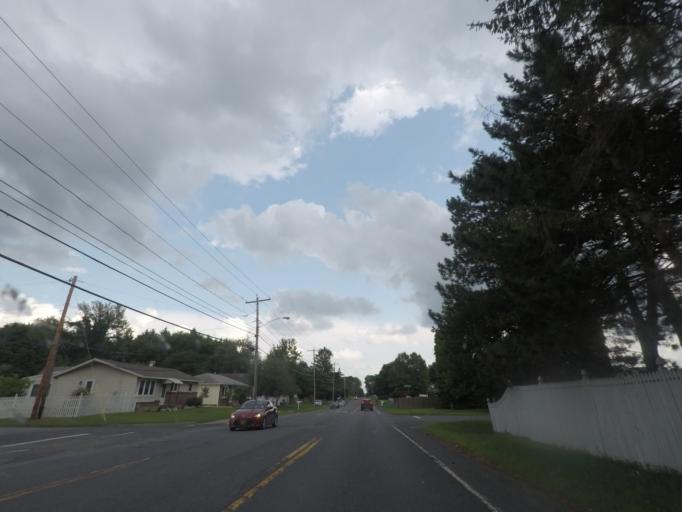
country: US
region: New York
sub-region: Albany County
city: Roessleville
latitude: 42.7020
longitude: -73.7968
